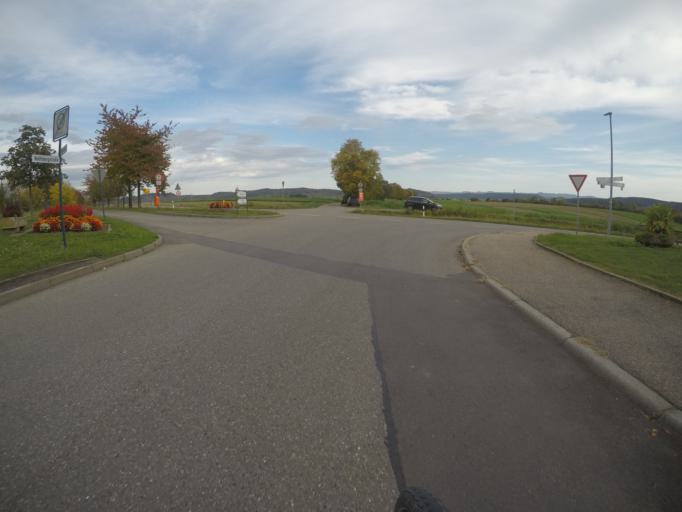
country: DE
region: Baden-Wuerttemberg
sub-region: Tuebingen Region
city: Rottenburg
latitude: 48.5431
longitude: 8.9259
